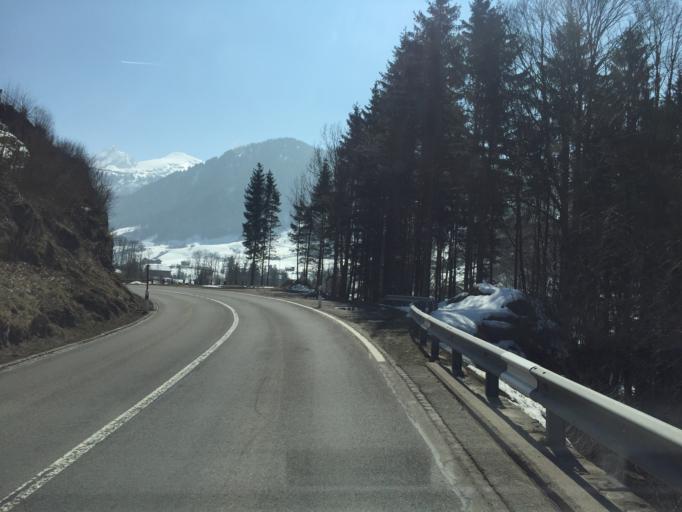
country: CH
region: Saint Gallen
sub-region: Wahlkreis Toggenburg
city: Krummenau
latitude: 47.2087
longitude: 9.2176
